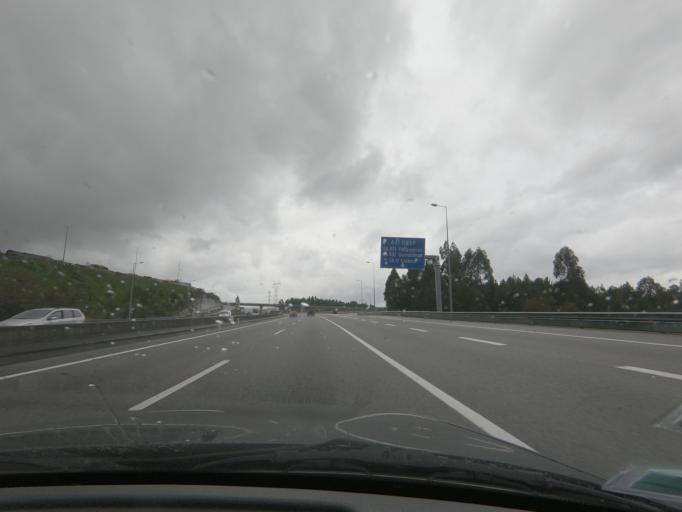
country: PT
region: Porto
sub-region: Valongo
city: Campo
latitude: 41.1778
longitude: -8.4422
